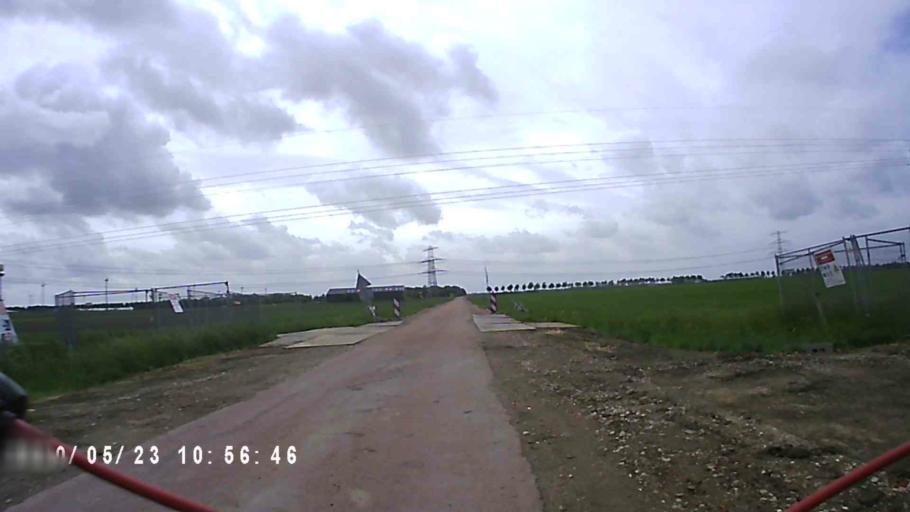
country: NL
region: Groningen
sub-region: Gemeente Delfzijl
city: Delfzijl
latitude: 53.3022
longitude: 6.9430
